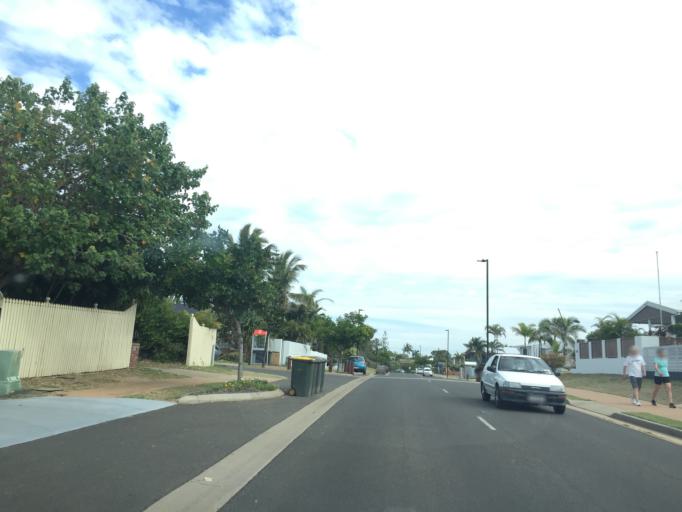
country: AU
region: Queensland
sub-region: Bundaberg
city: Bundaberg
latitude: -24.8234
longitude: 152.4652
